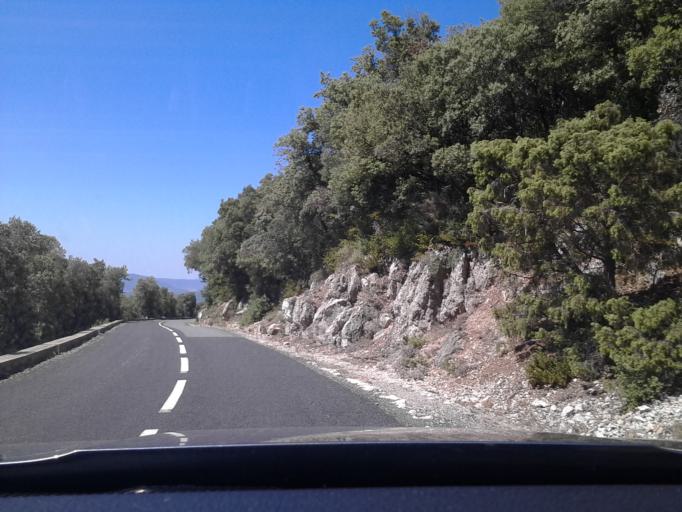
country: FR
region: Languedoc-Roussillon
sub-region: Departement de l'Herault
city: Montpeyroux
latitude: 43.7364
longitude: 3.4553
